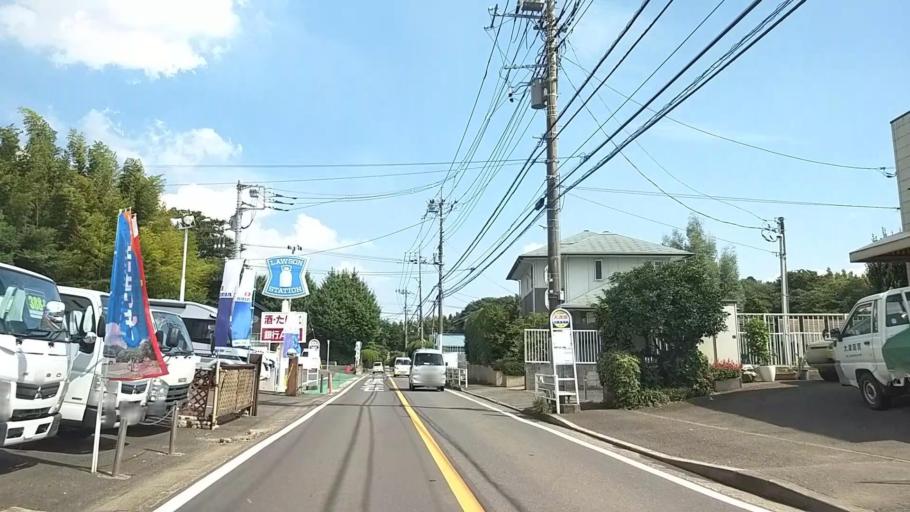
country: JP
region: Kanagawa
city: Yokohama
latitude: 35.5261
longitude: 139.5794
